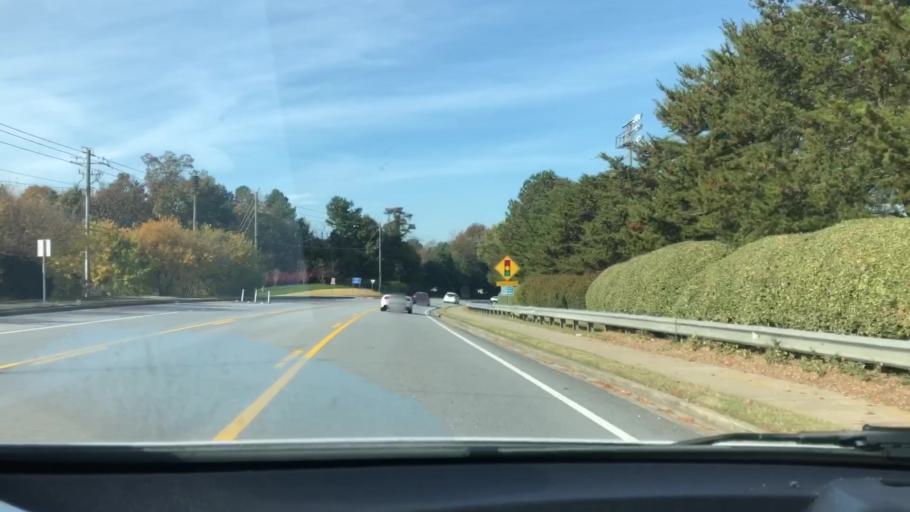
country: US
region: Georgia
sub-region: Gwinnett County
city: Norcross
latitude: 33.9678
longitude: -84.2147
